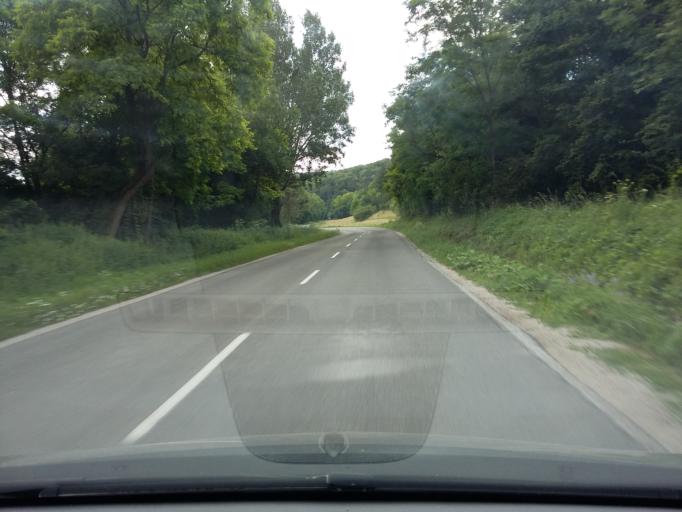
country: SK
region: Trnavsky
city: Smolenice
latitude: 48.5443
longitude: 17.4356
